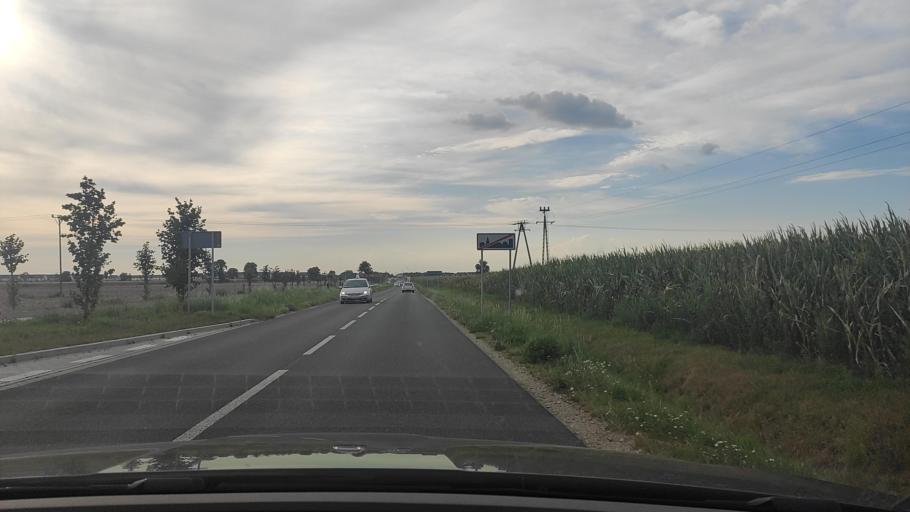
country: PL
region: Greater Poland Voivodeship
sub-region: Powiat poznanski
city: Kornik
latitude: 52.2938
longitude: 17.1053
